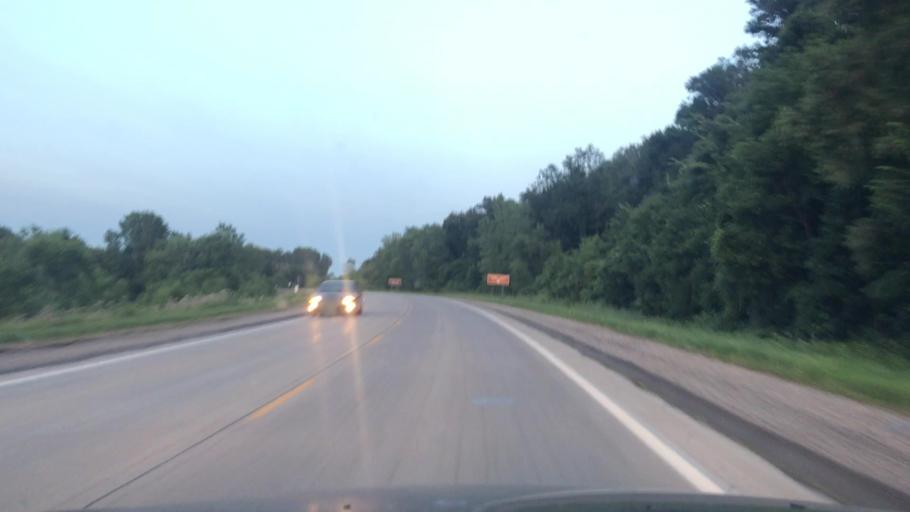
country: US
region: Minnesota
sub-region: Redwood County
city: Redwood Falls
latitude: 44.5405
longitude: -95.0117
